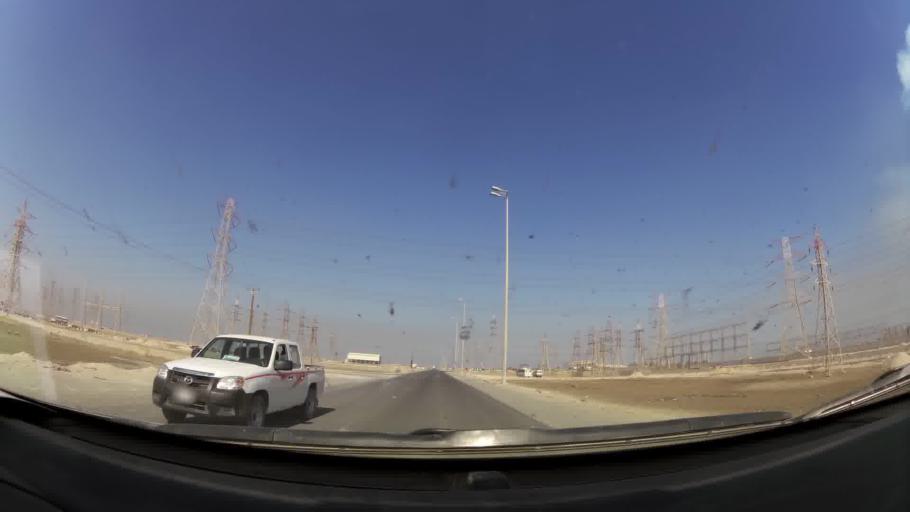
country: SA
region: Eastern Province
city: Al Khafji
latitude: 28.7097
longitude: 48.3616
